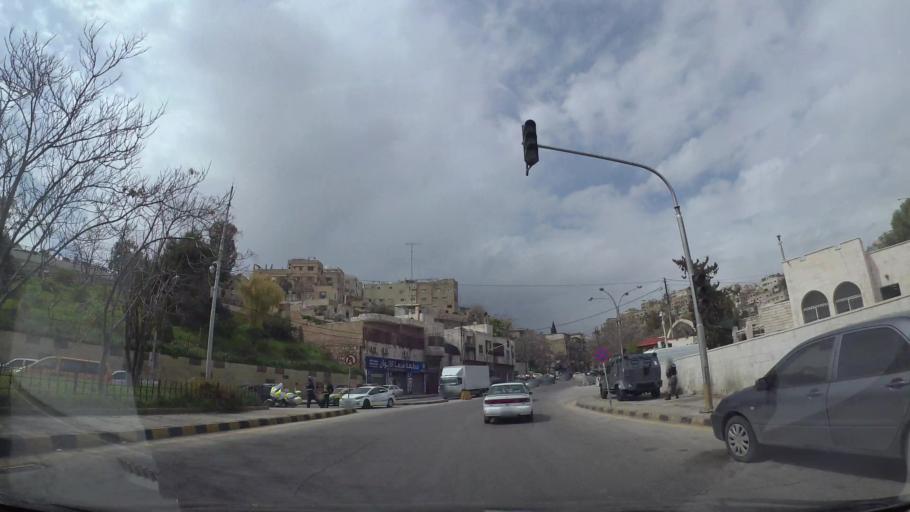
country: JO
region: Amman
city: Amman
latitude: 31.9545
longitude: 35.9448
